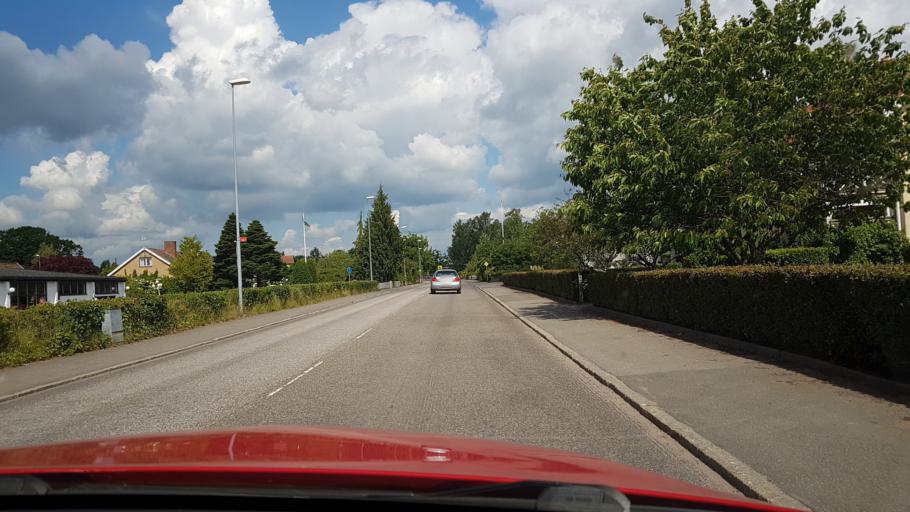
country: SE
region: Vaestra Goetaland
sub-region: Hjo Kommun
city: Hjo
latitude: 58.3096
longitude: 14.2831
